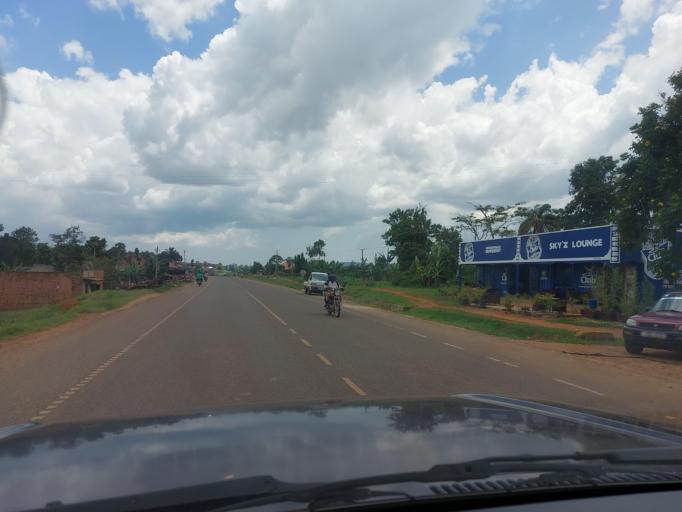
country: UG
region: Central Region
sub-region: Mukono District
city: Mukono
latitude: 0.3138
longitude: 32.7719
